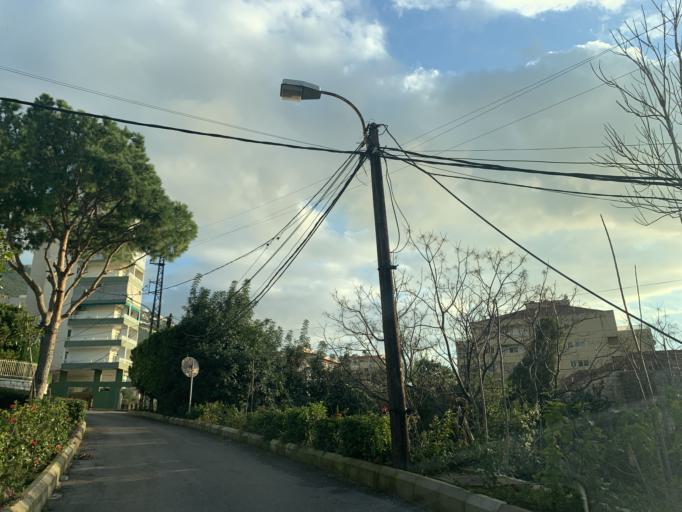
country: LB
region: Mont-Liban
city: Djounie
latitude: 33.9964
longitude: 35.6439
